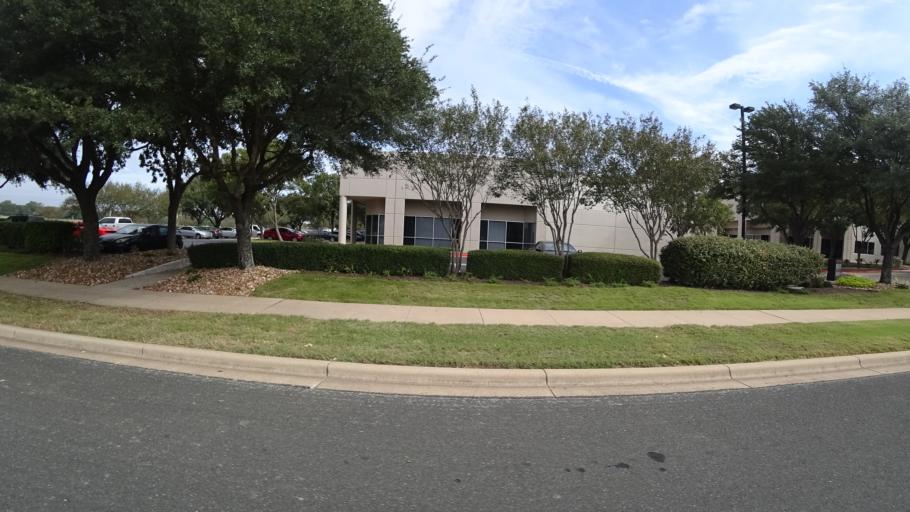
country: US
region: Texas
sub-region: Travis County
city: Austin
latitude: 30.2108
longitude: -97.7198
